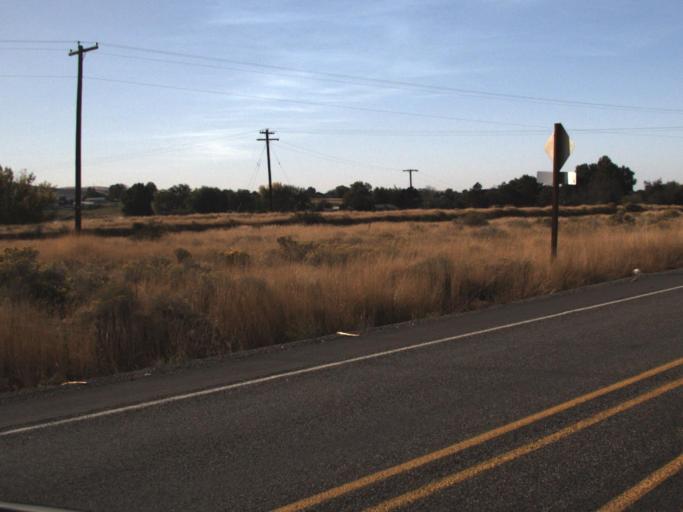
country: US
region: Washington
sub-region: Benton County
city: Finley
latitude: 46.1840
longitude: -119.0706
